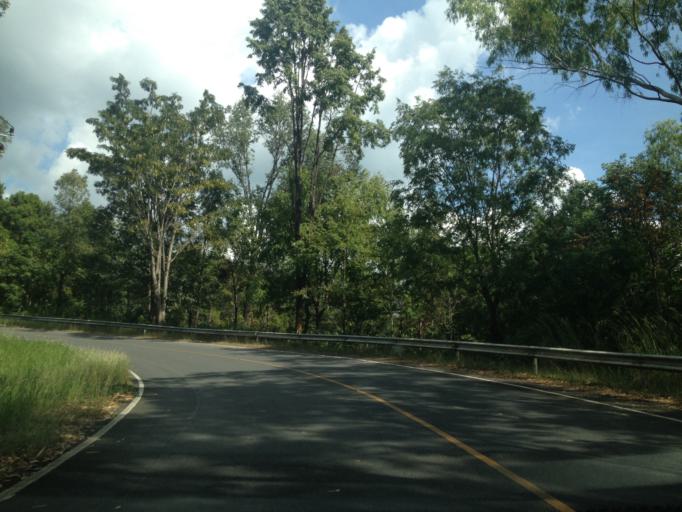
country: TH
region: Chiang Mai
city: Samoeng
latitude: 18.8333
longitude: 98.7833
